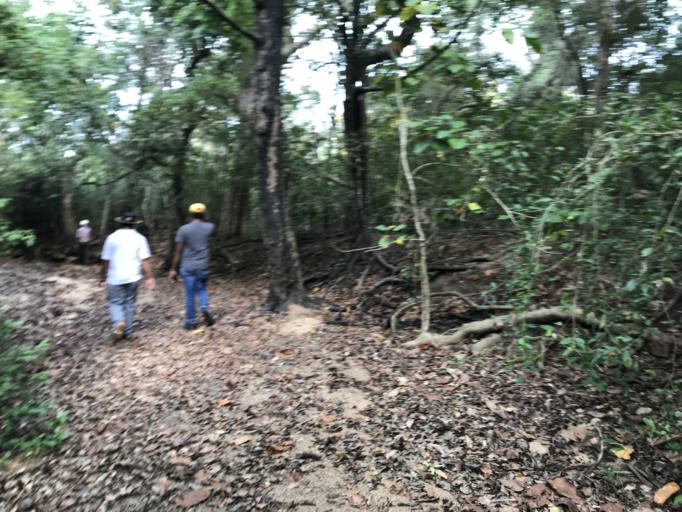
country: LK
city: Padaviya Divisional Secretariat
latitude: 9.0821
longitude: 80.8005
